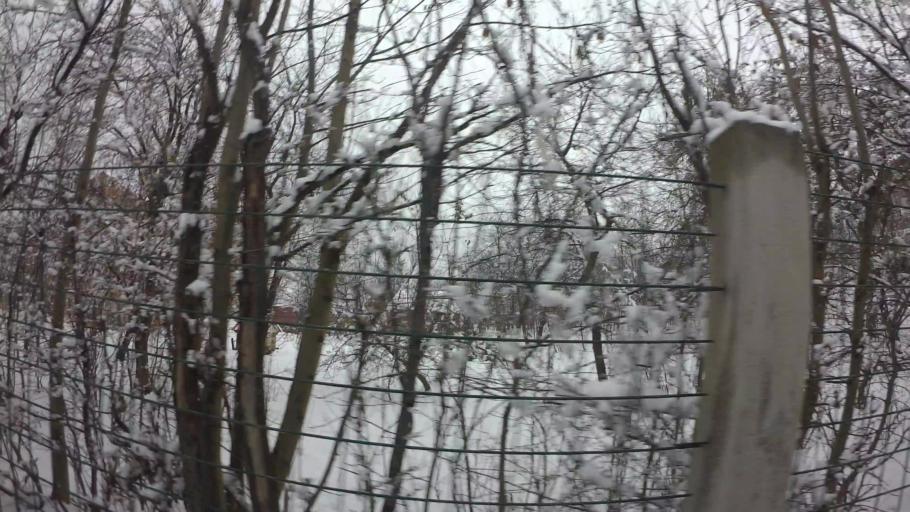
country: BA
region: Federation of Bosnia and Herzegovina
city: Kobilja Glava
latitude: 43.8495
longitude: 18.4183
